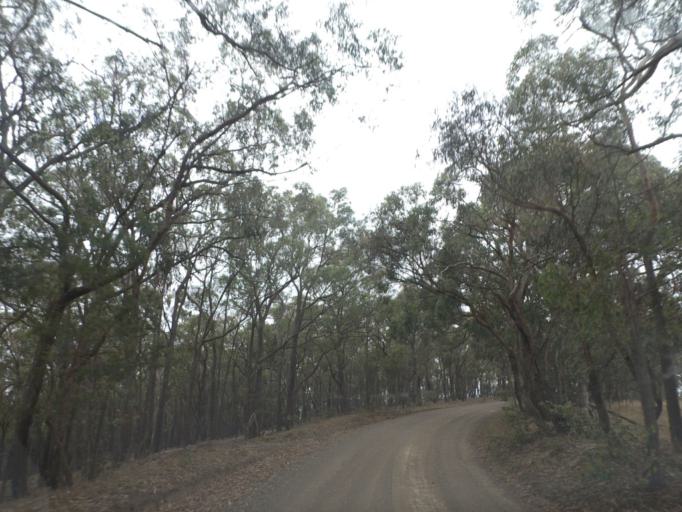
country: AU
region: Victoria
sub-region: Yarra Ranges
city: Yarra Glen
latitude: -37.6625
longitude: 145.3355
